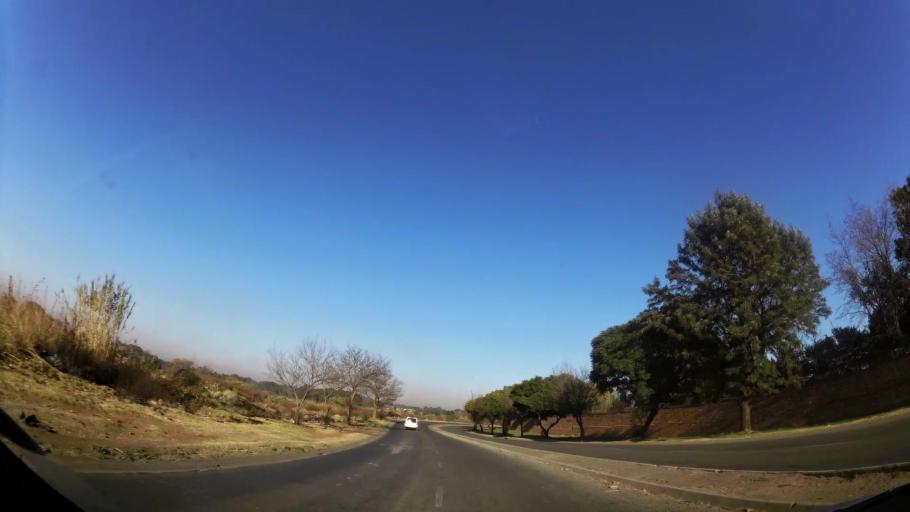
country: ZA
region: Gauteng
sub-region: Ekurhuleni Metropolitan Municipality
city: Germiston
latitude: -26.1940
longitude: 28.1593
